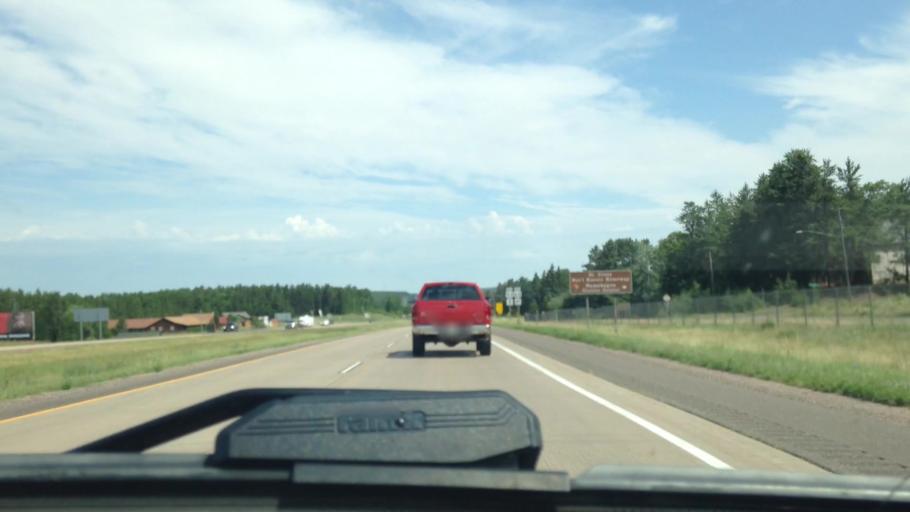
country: US
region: Wisconsin
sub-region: Washburn County
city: Spooner
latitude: 45.9018
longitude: -91.8278
